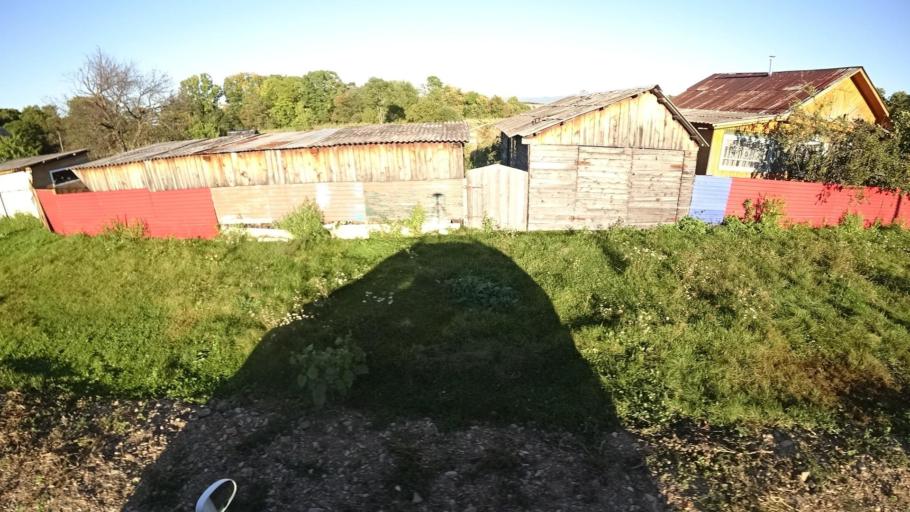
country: RU
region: Primorskiy
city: Kirovskiy
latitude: 44.8271
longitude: 133.5697
